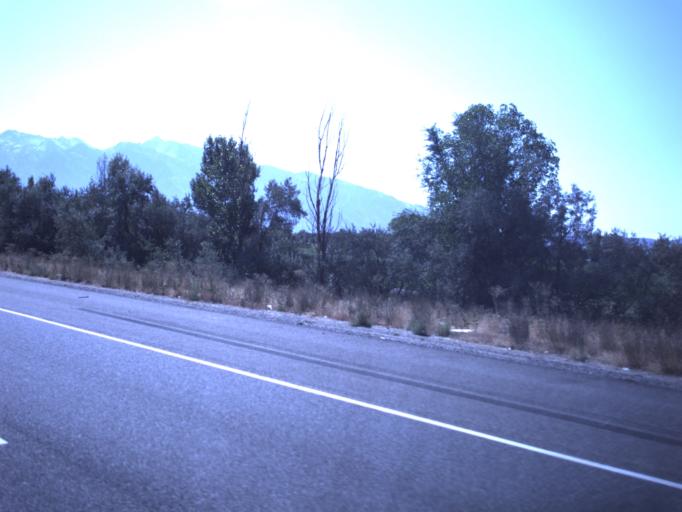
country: US
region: Utah
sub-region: Salt Lake County
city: Midvale
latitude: 40.6367
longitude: -111.9170
